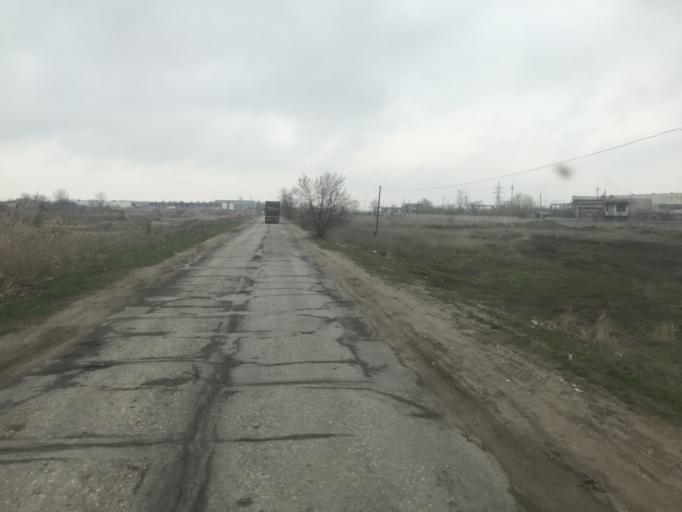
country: RU
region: Volgograd
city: Svetlyy Yar
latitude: 48.5208
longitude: 44.6233
